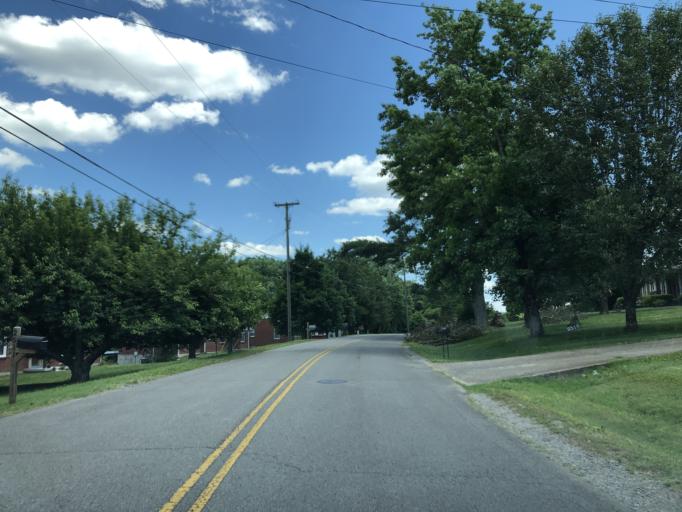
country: US
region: Tennessee
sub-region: Davidson County
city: Nashville
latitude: 36.1790
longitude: -86.7198
